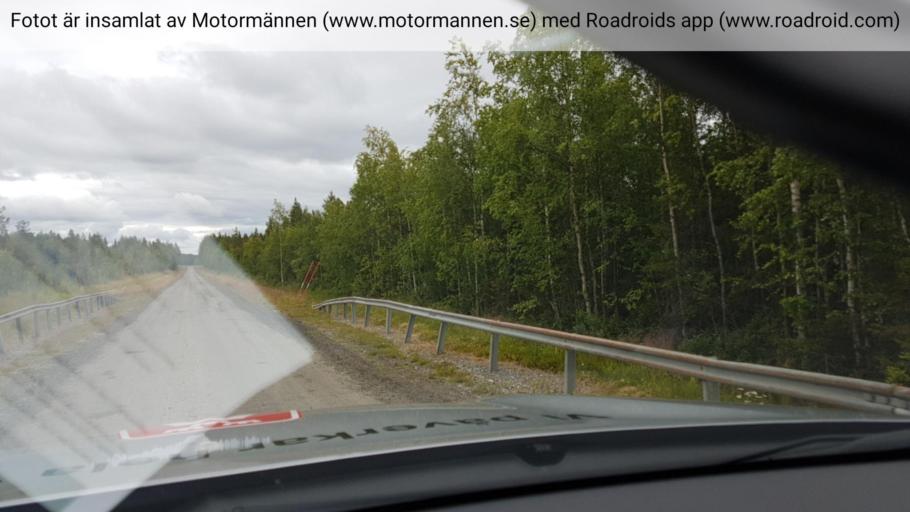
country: SE
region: Norrbotten
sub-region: Pajala Kommun
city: Pajala
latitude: 66.9807
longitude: 22.8829
